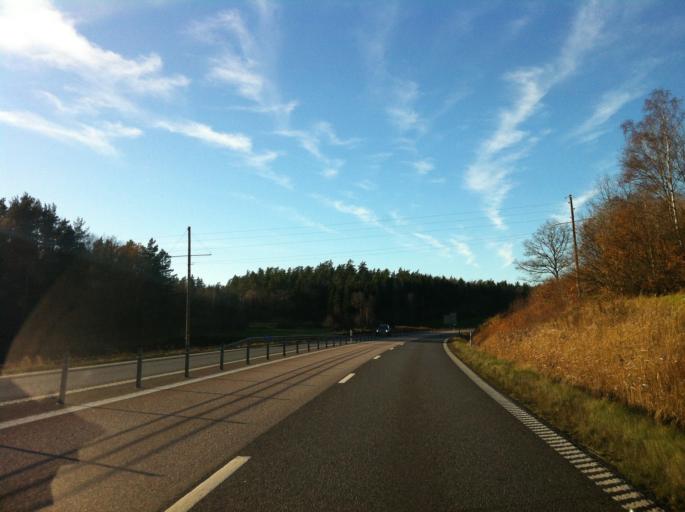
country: SE
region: Blekinge
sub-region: Karlshamns Kommun
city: Karlshamn
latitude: 56.1872
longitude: 14.9101
